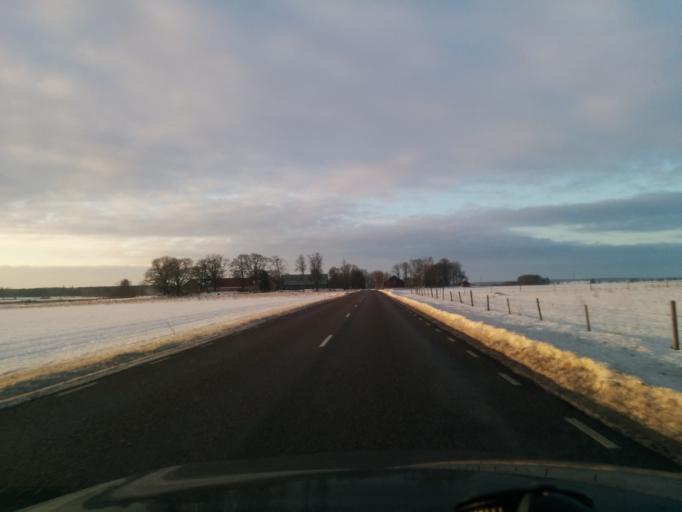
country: SE
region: Uppsala
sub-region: Tierps Kommun
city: Orbyhus
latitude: 60.1799
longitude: 17.6624
